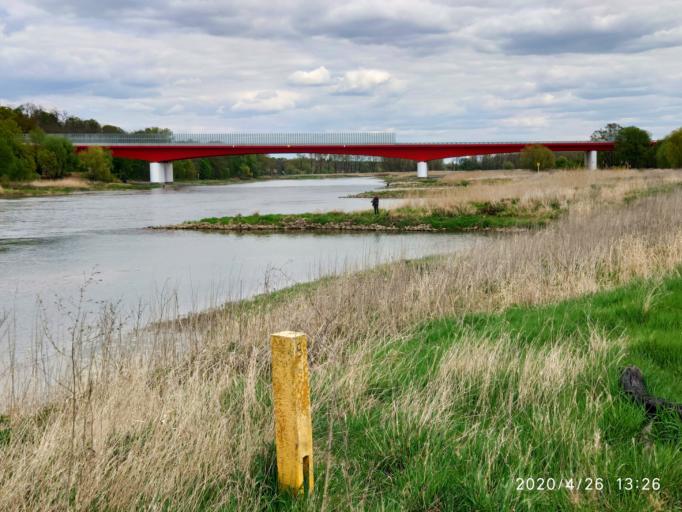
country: PL
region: Lubusz
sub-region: Powiat zielonogorski
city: Sulechow
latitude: 52.0299
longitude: 15.6207
